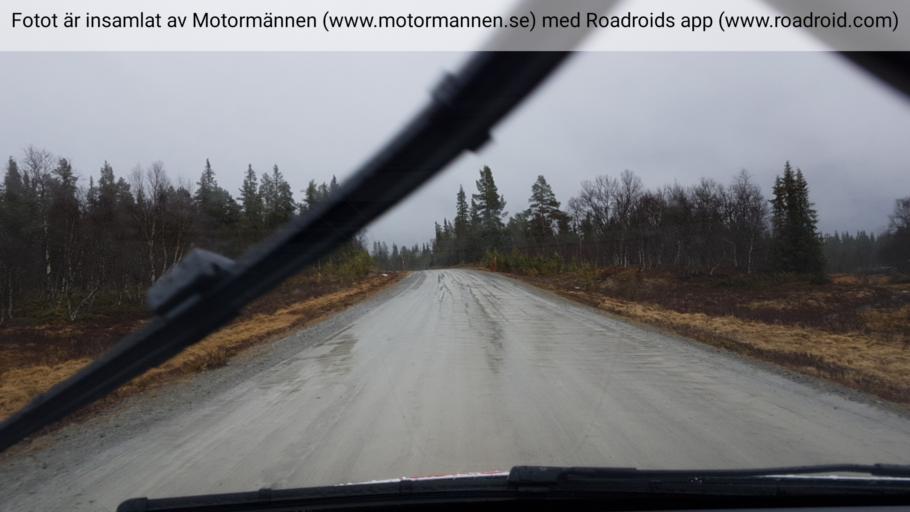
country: SE
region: Jaemtland
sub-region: Are Kommun
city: Are
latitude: 62.6661
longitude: 12.9232
